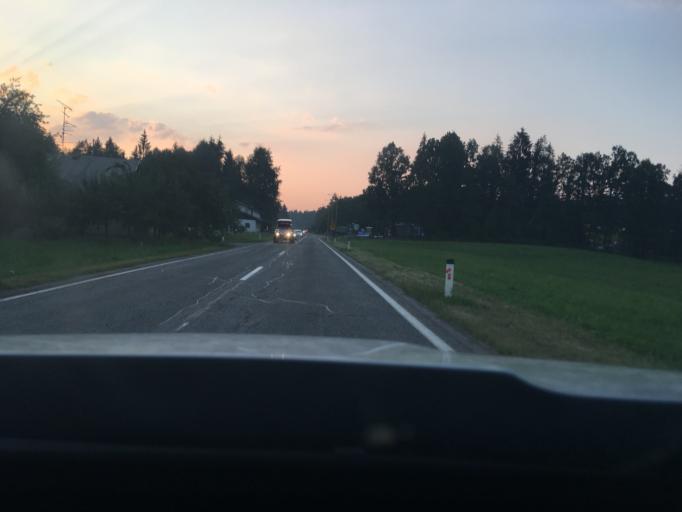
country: SI
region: Kocevje
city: Kocevje
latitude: 45.6751
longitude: 14.8281
